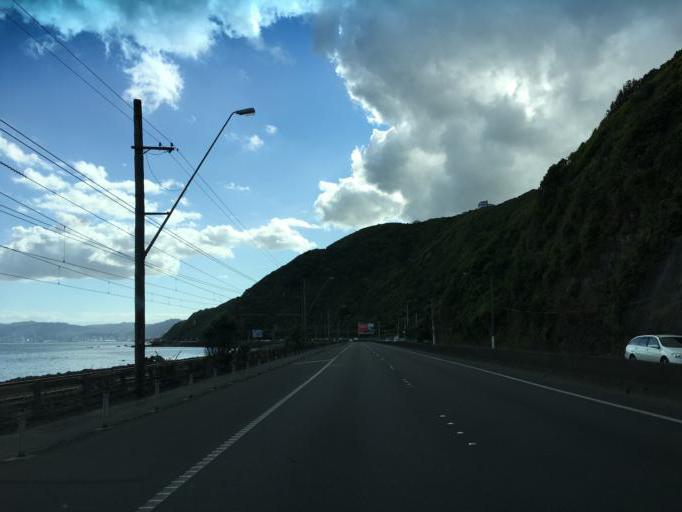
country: NZ
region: Wellington
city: Petone
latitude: -41.2278
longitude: 174.8473
